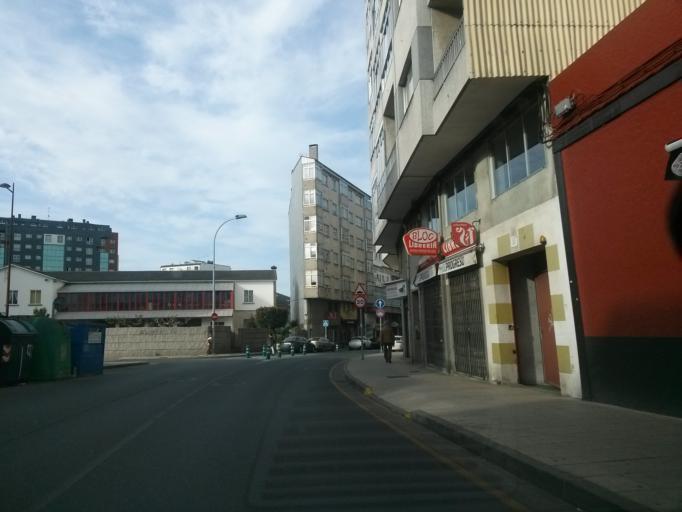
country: ES
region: Galicia
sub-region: Provincia de Lugo
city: Lugo
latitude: 43.0199
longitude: -7.5655
